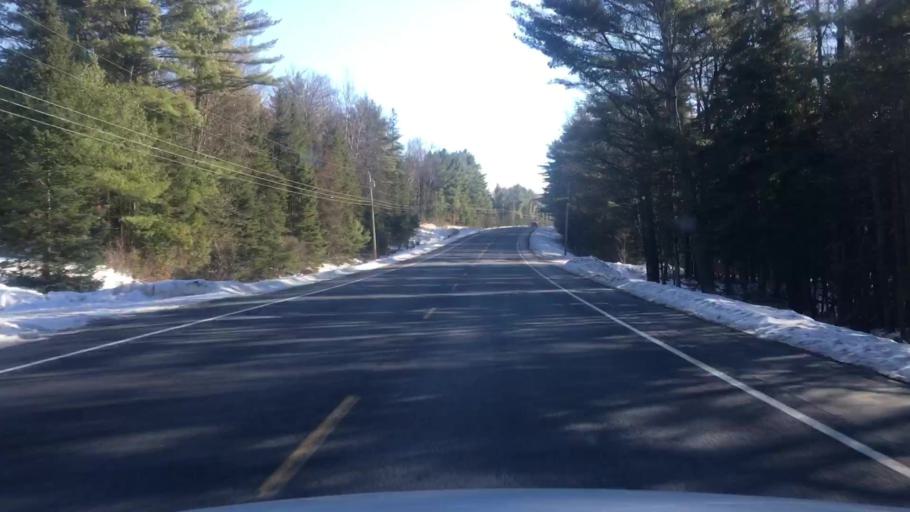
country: US
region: Maine
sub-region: Somerset County
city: Madison
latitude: 44.9236
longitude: -69.8279
